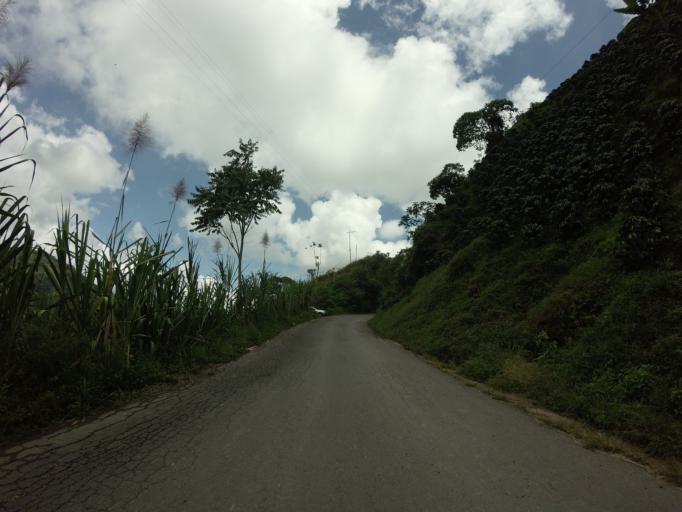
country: CO
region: Caldas
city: Marquetalia
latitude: 5.2992
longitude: -75.0671
